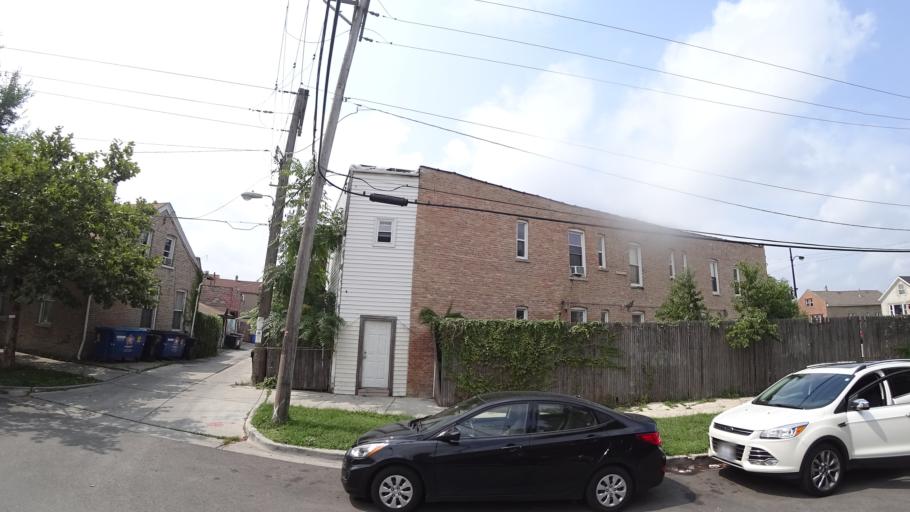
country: US
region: Illinois
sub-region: Cook County
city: Chicago
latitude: 41.8481
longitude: -87.6782
